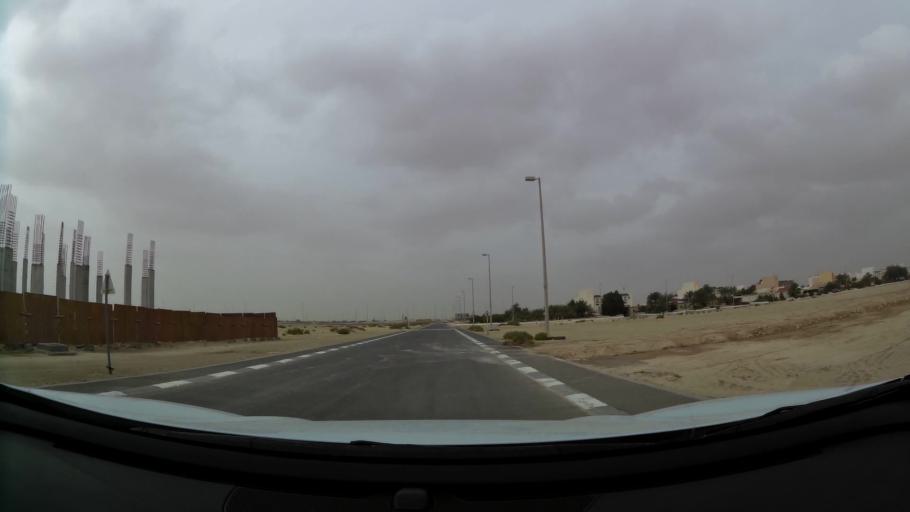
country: AE
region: Abu Dhabi
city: Abu Dhabi
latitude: 24.3654
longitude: 54.6650
